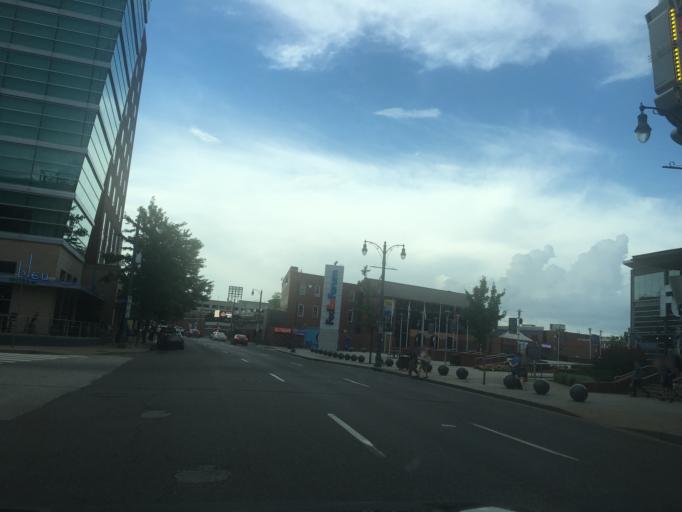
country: US
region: Tennessee
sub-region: Shelby County
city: Memphis
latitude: 35.1384
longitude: -90.0524
